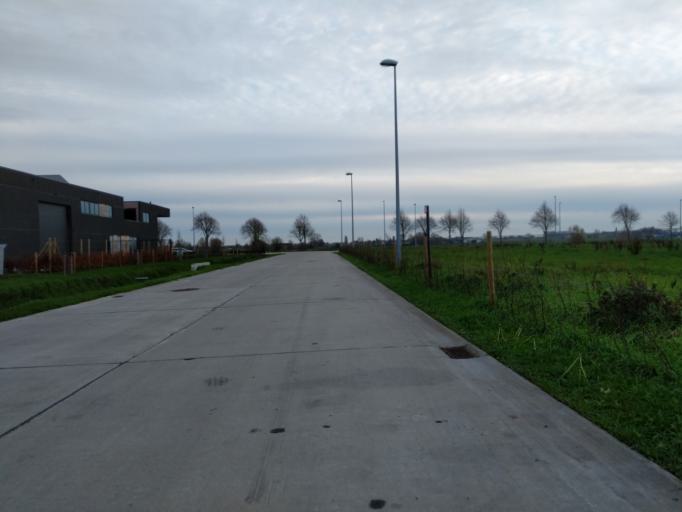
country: BE
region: Flanders
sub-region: Provincie West-Vlaanderen
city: Ruiselede
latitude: 51.0381
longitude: 3.4037
